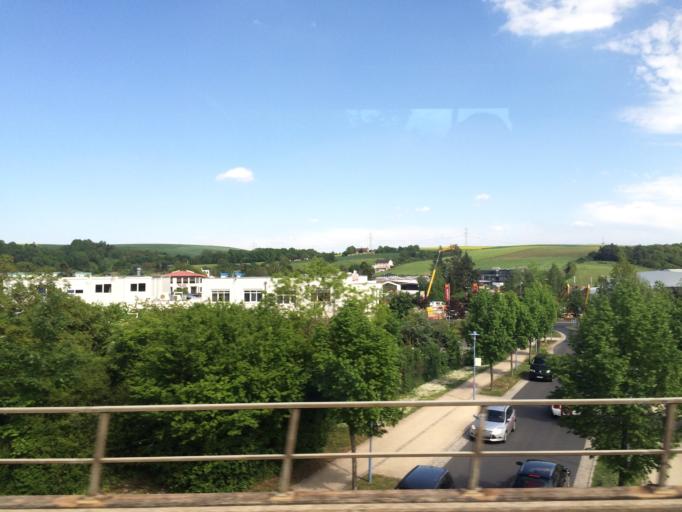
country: DE
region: Bavaria
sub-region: Regierungsbezirk Unterfranken
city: Rottendorf
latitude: 49.7902
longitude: 10.0293
